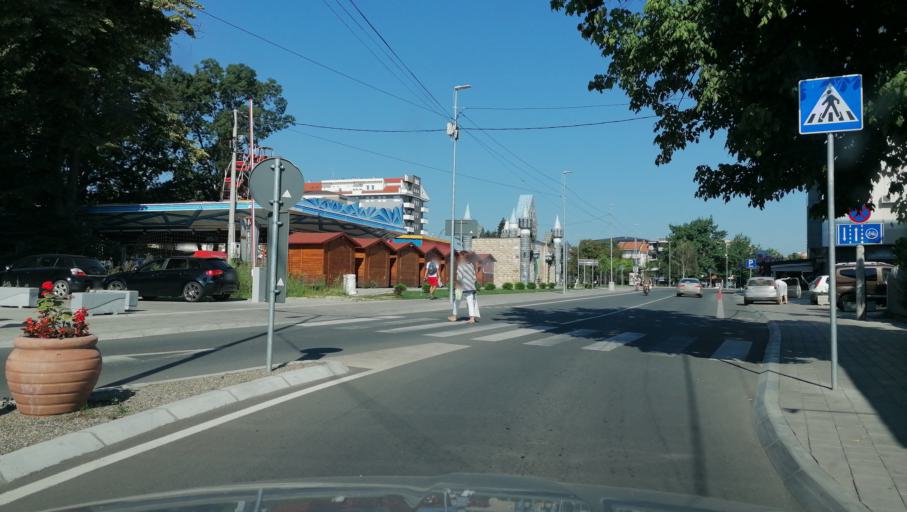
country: RS
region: Central Serbia
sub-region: Rasinski Okrug
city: Krusevac
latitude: 43.5764
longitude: 21.3335
